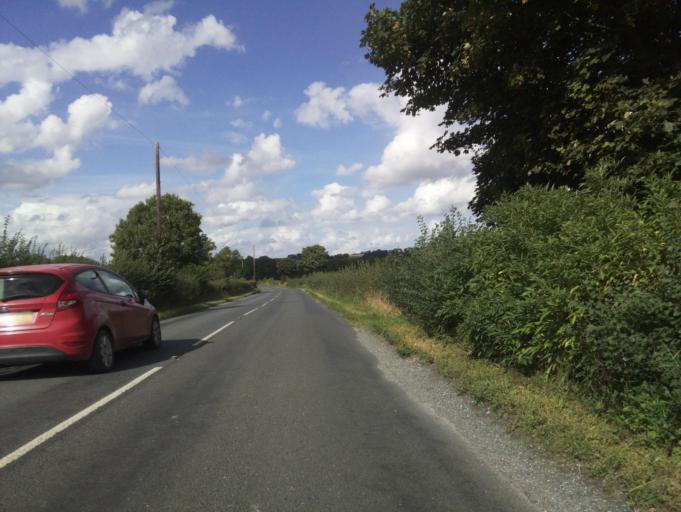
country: GB
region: England
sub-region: North Yorkshire
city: Leyburn
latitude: 54.2741
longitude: -1.7792
